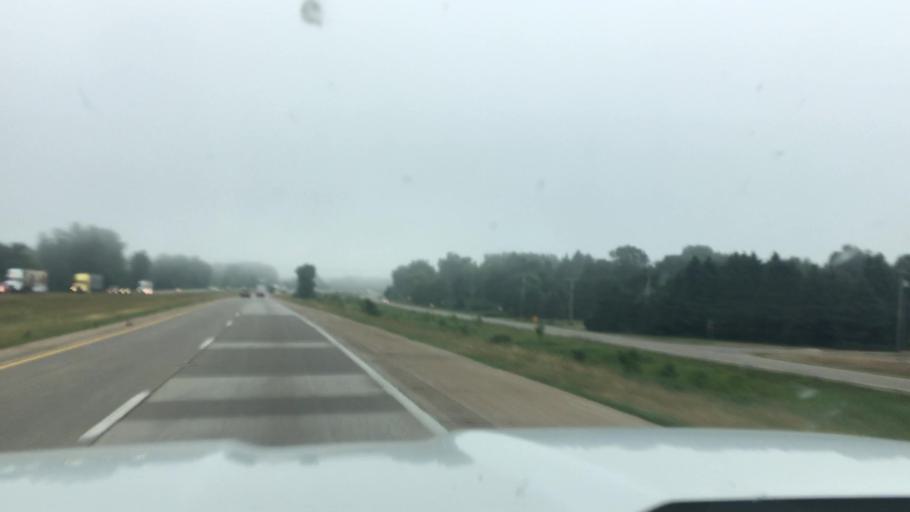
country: US
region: Michigan
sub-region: Shiawassee County
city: Perry
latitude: 42.8206
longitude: -84.2694
